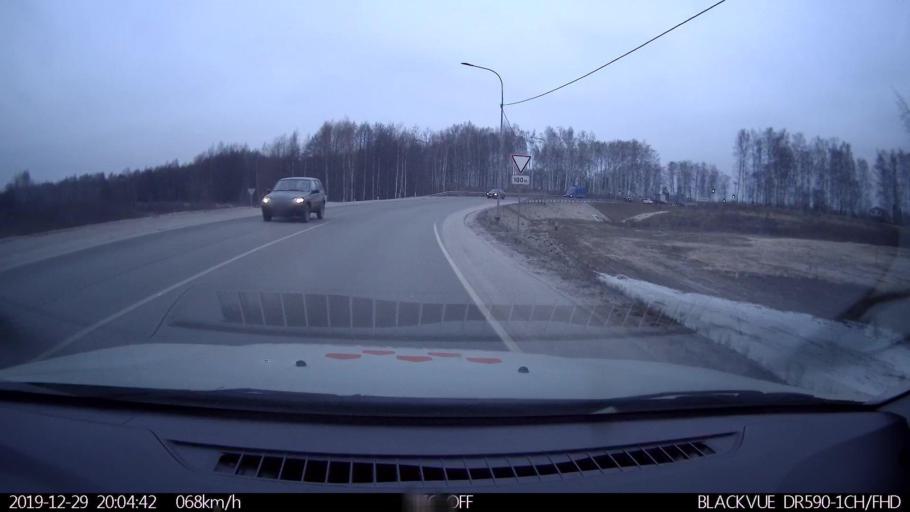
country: RU
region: Nizjnij Novgorod
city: Neklyudovo
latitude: 56.3867
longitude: 44.0091
